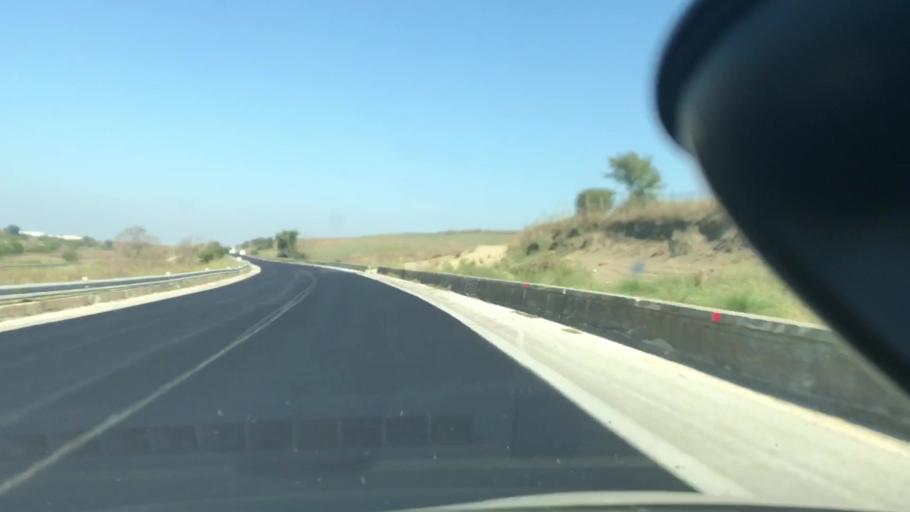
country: IT
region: Apulia
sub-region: Provincia di Barletta - Andria - Trani
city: Spinazzola
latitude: 40.9016
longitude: 16.1198
